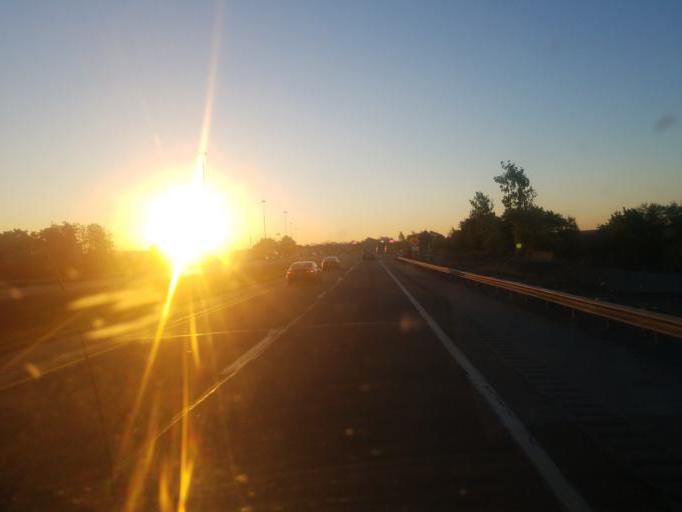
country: US
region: Ohio
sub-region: Mahoning County
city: New Middletown
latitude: 40.9256
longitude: -80.5601
